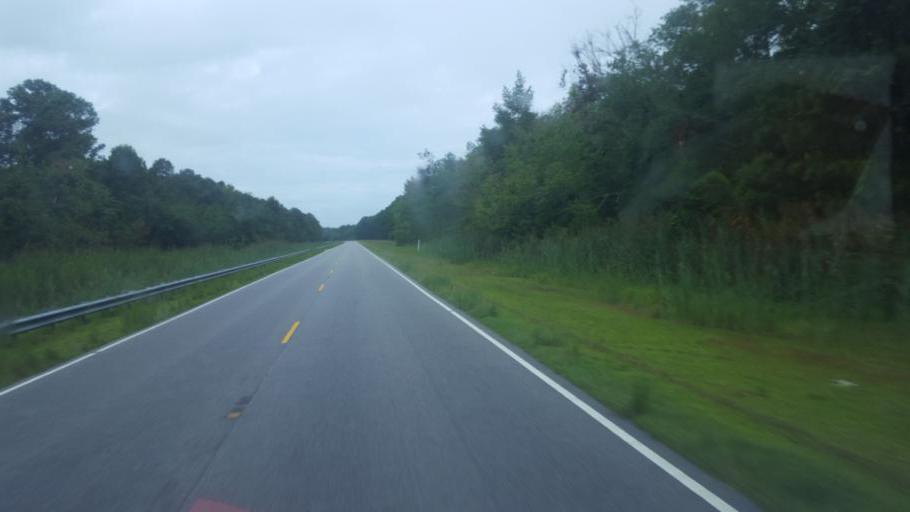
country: US
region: North Carolina
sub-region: Tyrrell County
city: Columbia
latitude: 35.9278
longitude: -76.1409
